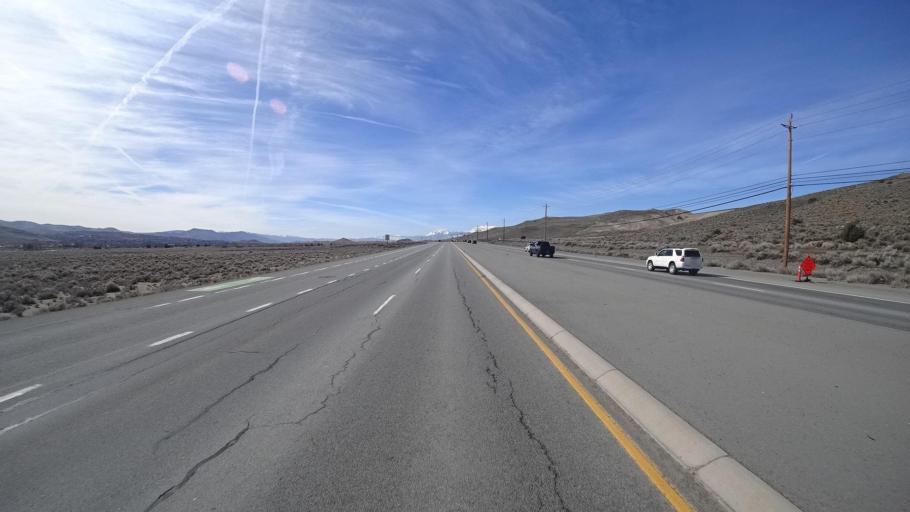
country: US
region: Nevada
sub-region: Washoe County
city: Spanish Springs
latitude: 39.6131
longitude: -119.7300
